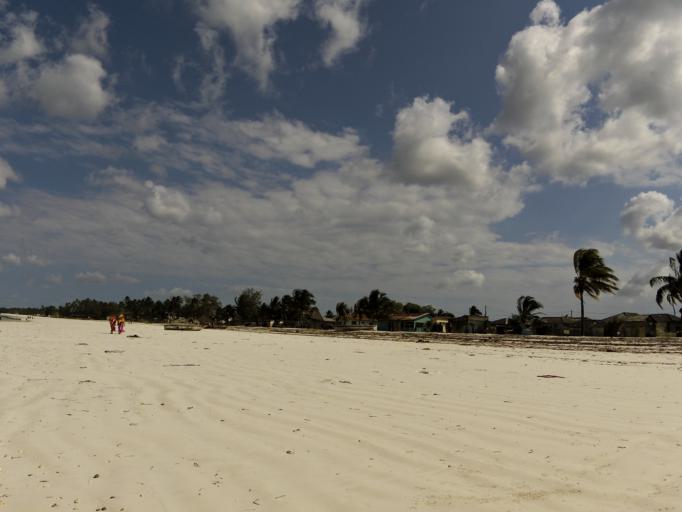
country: TZ
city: Kiwengwa
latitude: -6.0917
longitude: 39.4260
